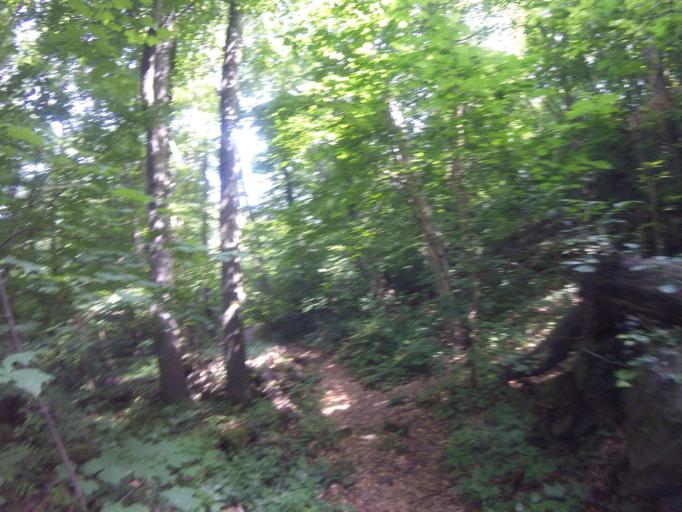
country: HU
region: Zala
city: Turje
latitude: 46.9116
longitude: 17.1738
